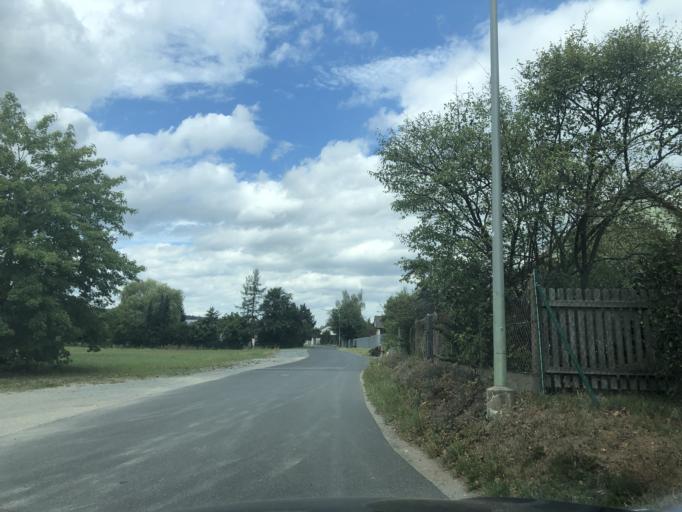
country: DE
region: Bavaria
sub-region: Upper Palatinate
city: Pressath
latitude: 49.7617
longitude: 11.9392
